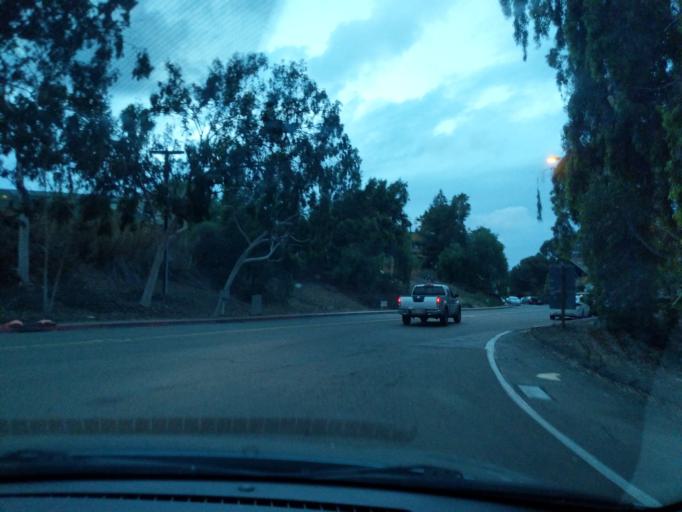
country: US
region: California
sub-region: San Diego County
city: San Diego
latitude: 32.7154
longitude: -117.1270
